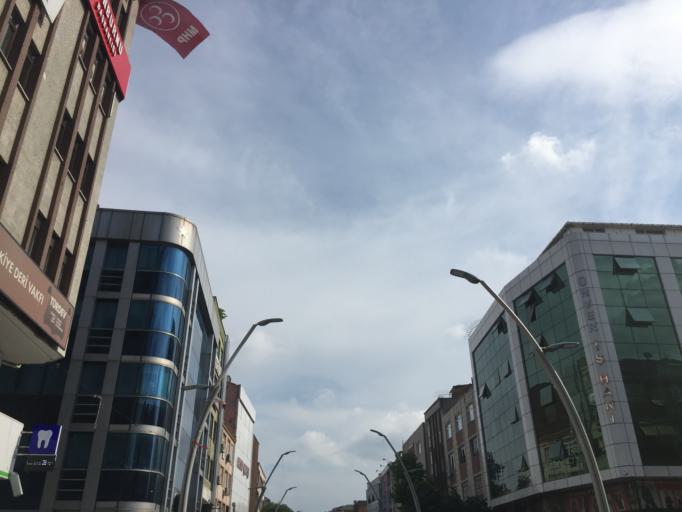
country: TR
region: Istanbul
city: Zeytinburnu
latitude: 40.9915
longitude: 28.9038
